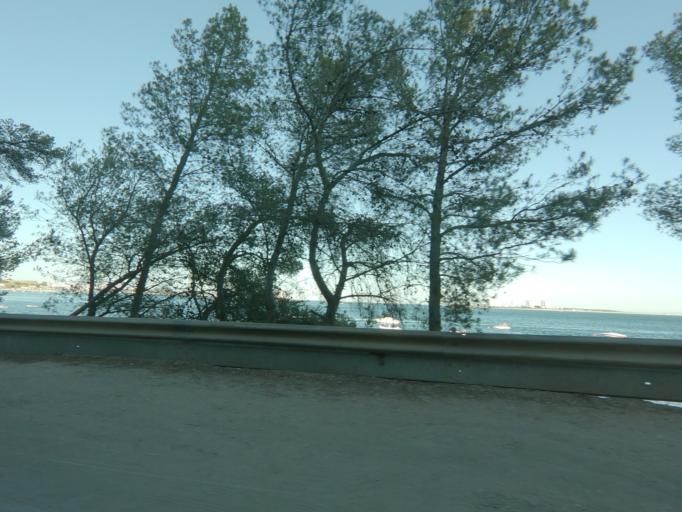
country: PT
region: Setubal
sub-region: Setubal
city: Setubal
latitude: 38.5047
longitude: -8.9263
